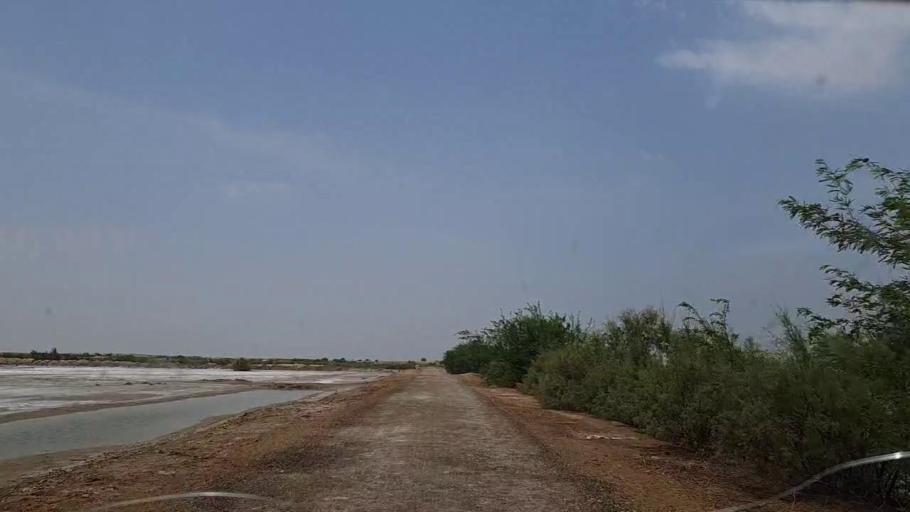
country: PK
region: Sindh
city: Phulji
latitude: 26.8693
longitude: 67.6529
